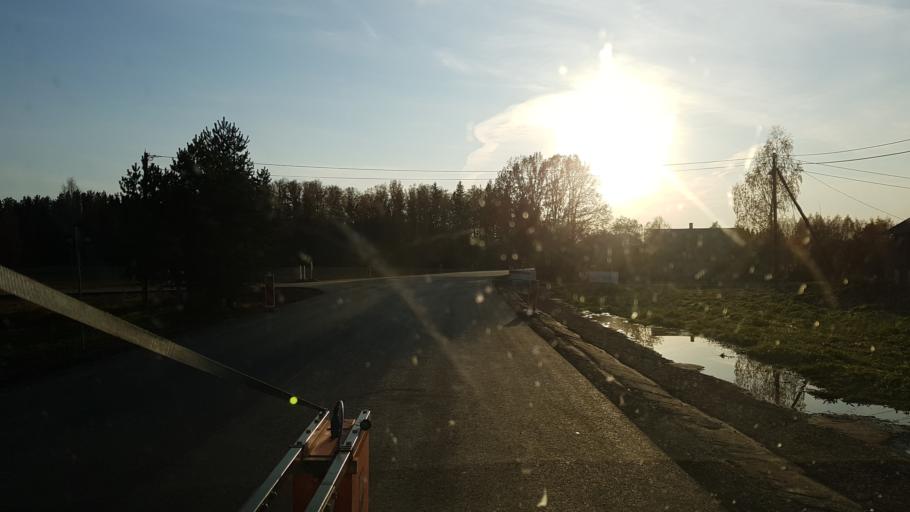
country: EE
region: Polvamaa
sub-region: Polva linn
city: Polva
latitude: 57.9448
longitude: 27.2134
